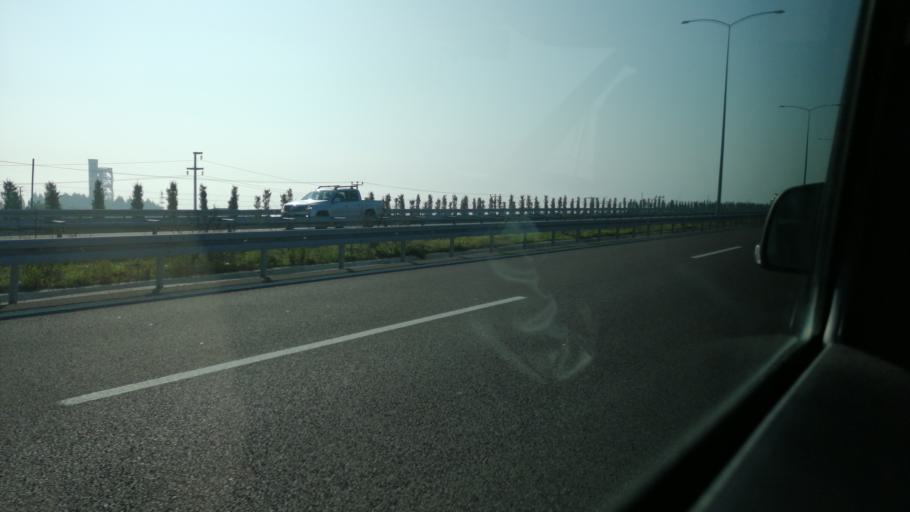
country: TR
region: Yalova
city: Altinova
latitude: 40.7232
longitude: 29.5027
